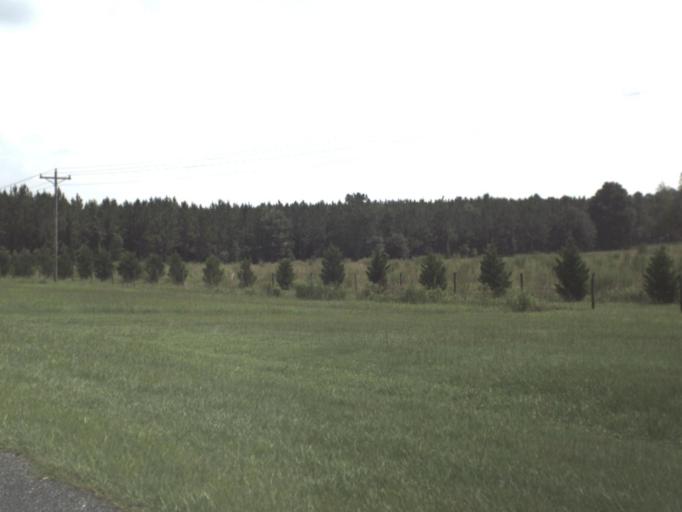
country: US
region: Florida
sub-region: Alachua County
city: High Springs
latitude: 29.9142
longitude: -82.6094
